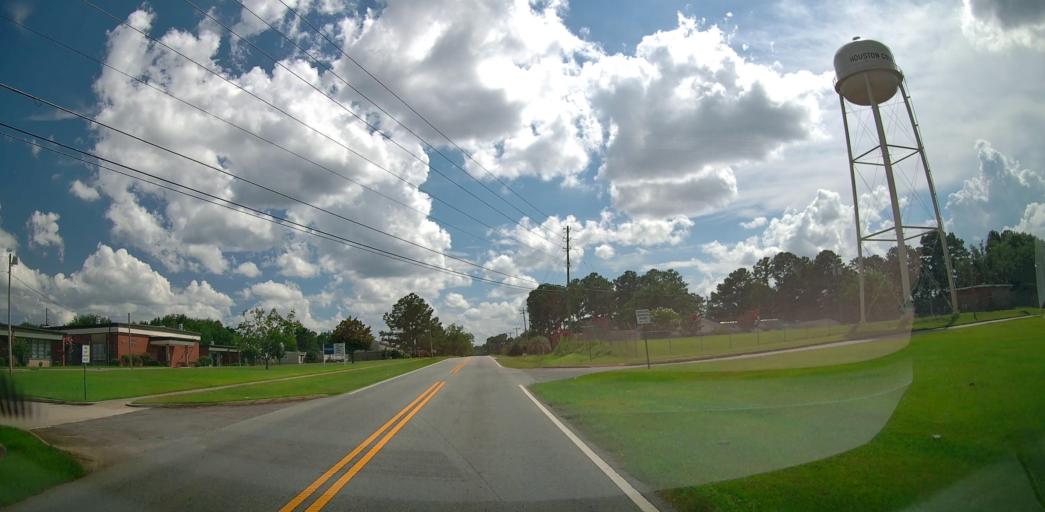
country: US
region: Georgia
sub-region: Houston County
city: Warner Robins
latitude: 32.6539
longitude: -83.6238
